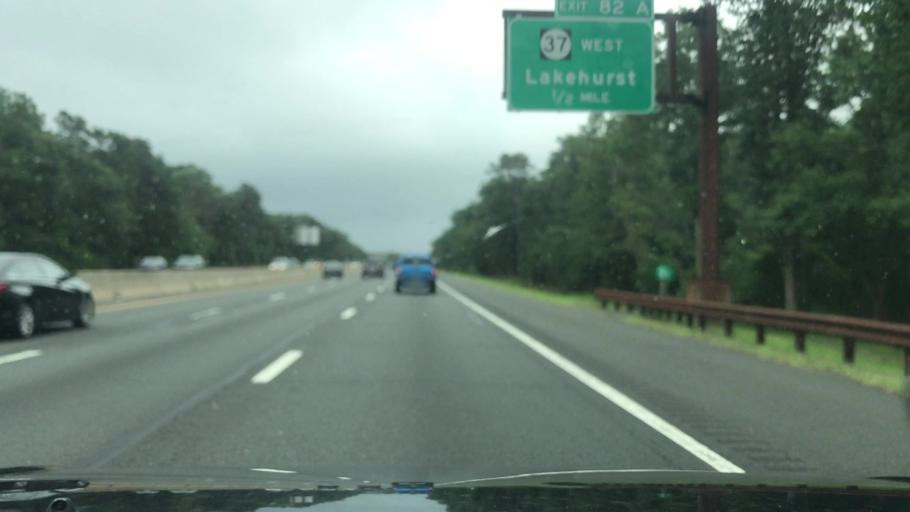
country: US
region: New Jersey
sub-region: Ocean County
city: Silver Ridge
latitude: 39.9735
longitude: -74.2104
